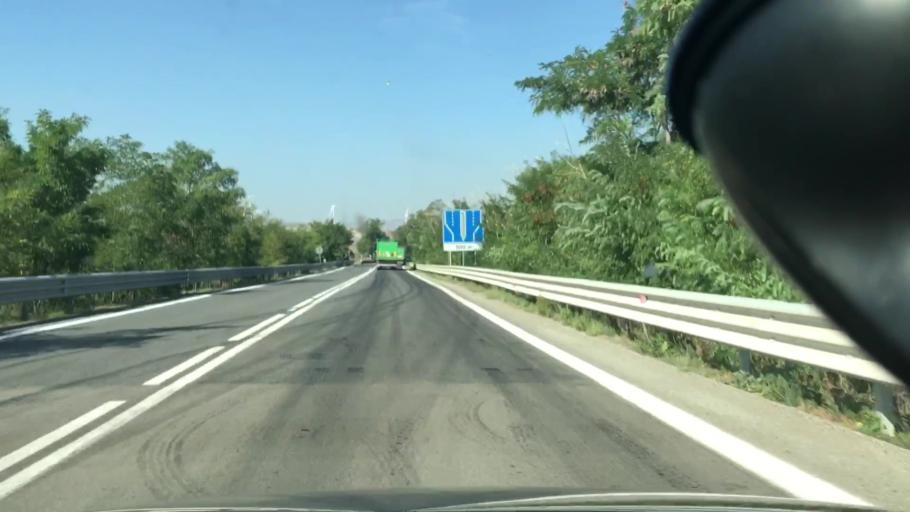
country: IT
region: Basilicate
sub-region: Provincia di Potenza
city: Zona 179
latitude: 41.0823
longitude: 15.6150
